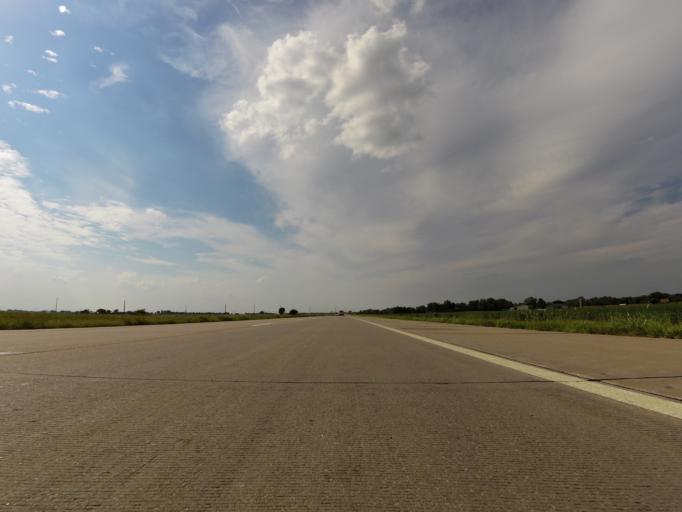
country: US
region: Kansas
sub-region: Sedgwick County
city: Colwich
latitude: 37.8184
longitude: -97.5088
